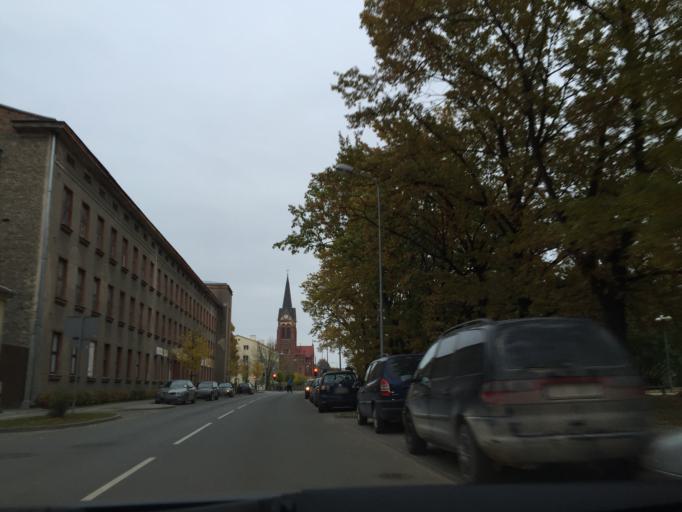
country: LV
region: Jelgava
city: Jelgava
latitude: 56.6483
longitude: 23.7226
